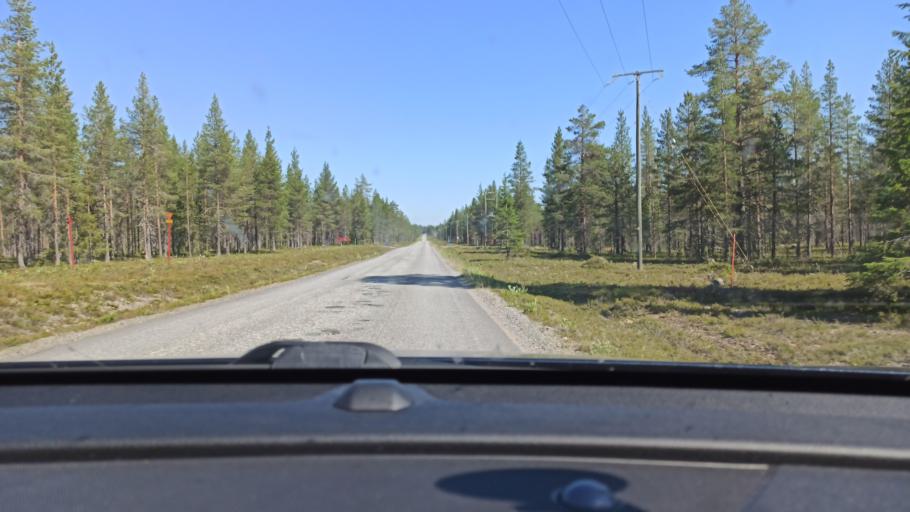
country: FI
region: Lapland
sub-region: Tunturi-Lappi
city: Kolari
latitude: 67.6459
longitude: 24.1601
